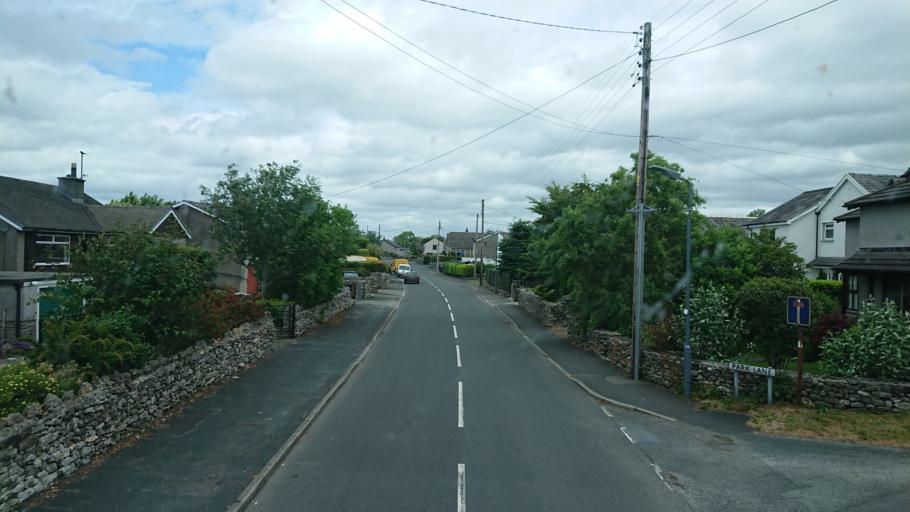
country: GB
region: England
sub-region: Cumbria
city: Milnthorpe
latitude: 54.2078
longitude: -2.7292
